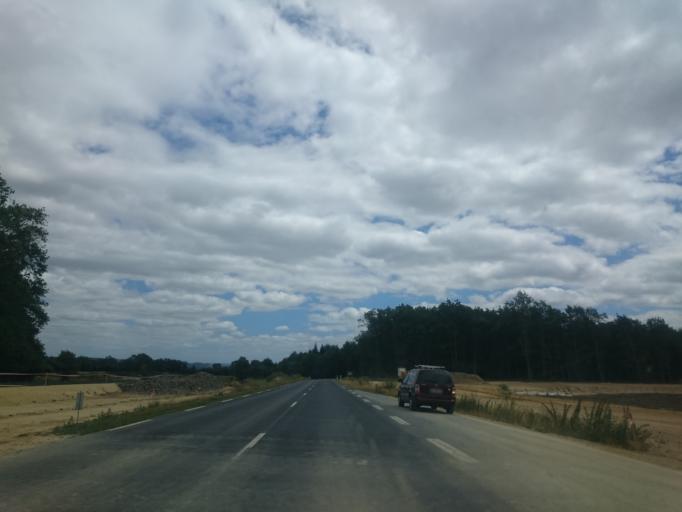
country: FR
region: Auvergne
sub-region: Departement du Cantal
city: Laroquebrou
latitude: 44.9696
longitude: 2.2367
